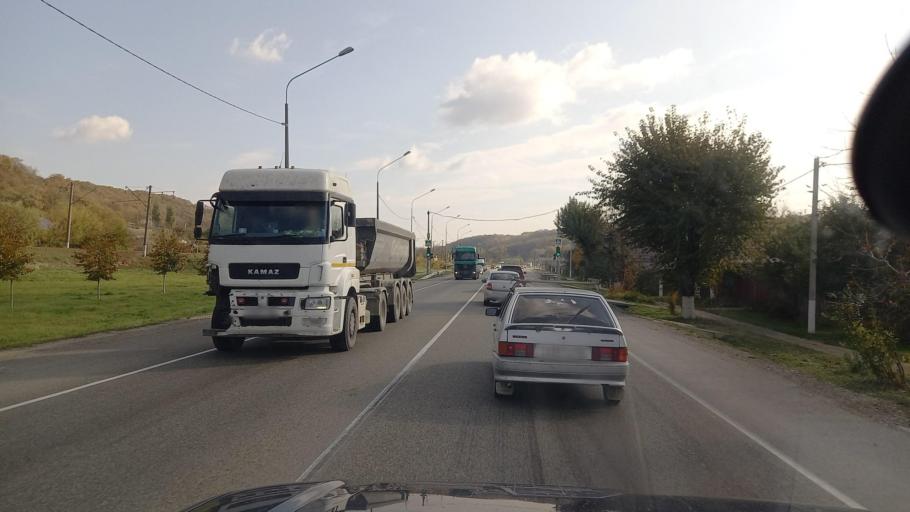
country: RU
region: Krasnodarskiy
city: Krymsk
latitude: 44.8692
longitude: 37.8779
